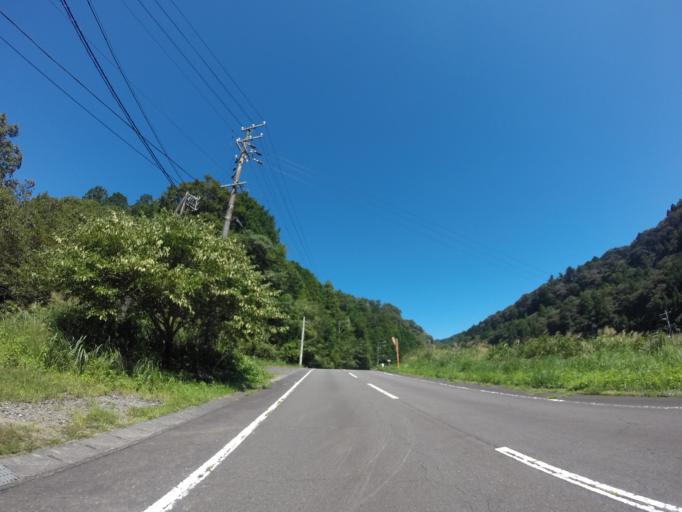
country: JP
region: Shizuoka
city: Fujieda
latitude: 34.9718
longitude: 138.1938
